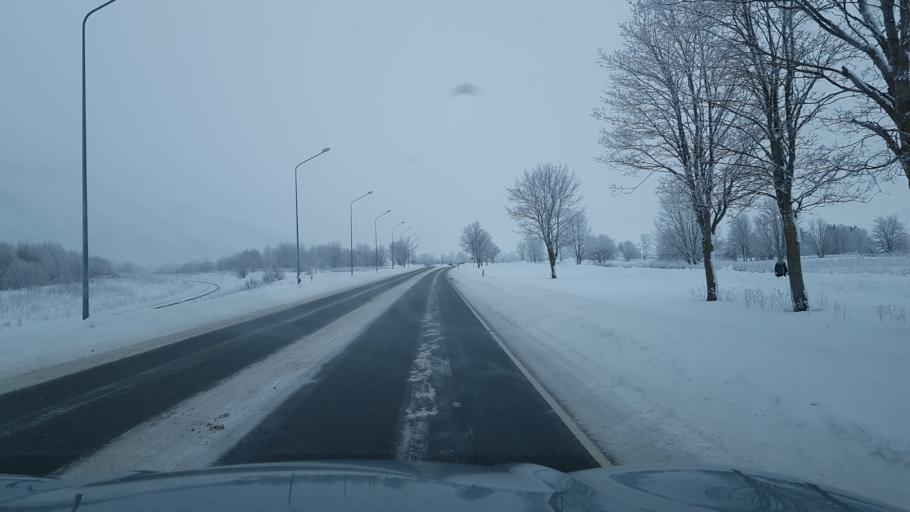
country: EE
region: Ida-Virumaa
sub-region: Johvi vald
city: Johvi
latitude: 59.3414
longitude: 27.4035
